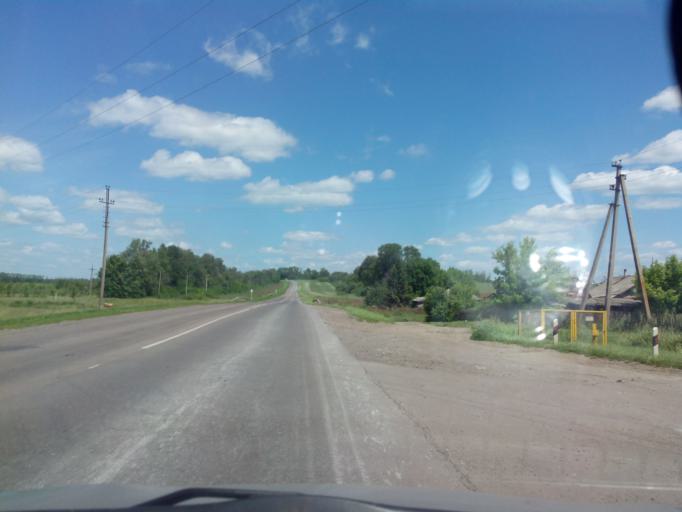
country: RU
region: Tambov
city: Zherdevka
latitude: 51.8390
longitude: 41.5097
